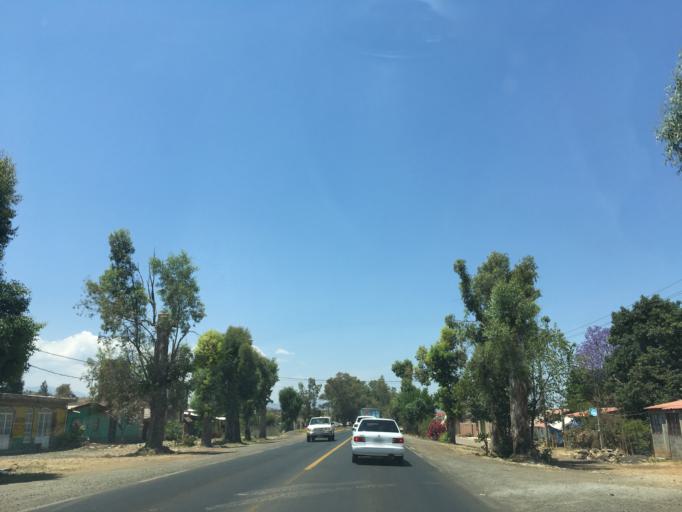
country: MX
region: Mexico
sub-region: Chalco
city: Santo Tomas
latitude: 19.8433
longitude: -102.0830
